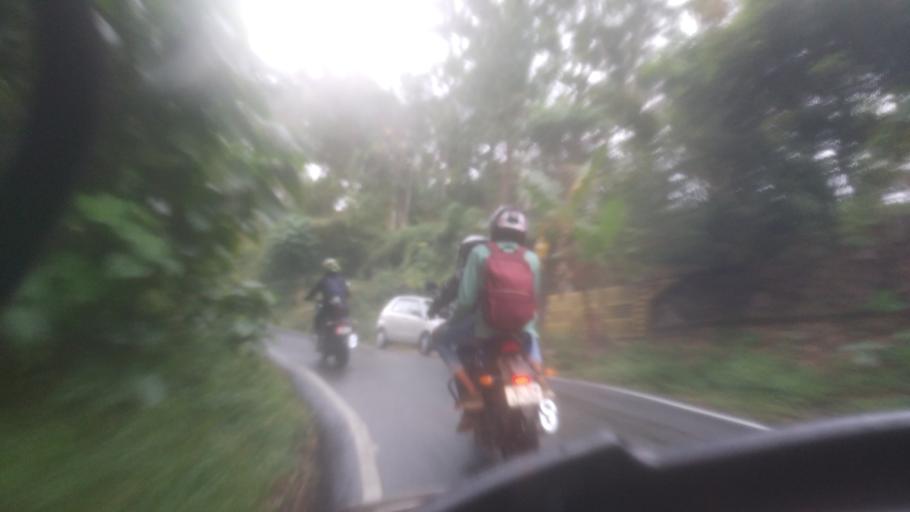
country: IN
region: Kerala
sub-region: Idukki
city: Idukki
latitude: 9.9293
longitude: 77.0733
